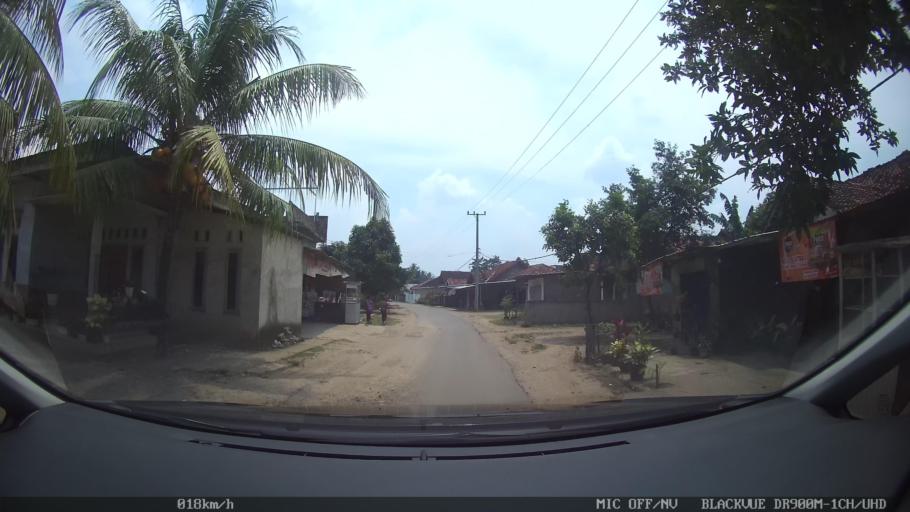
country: ID
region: Lampung
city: Natar
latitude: -5.3128
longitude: 105.2257
